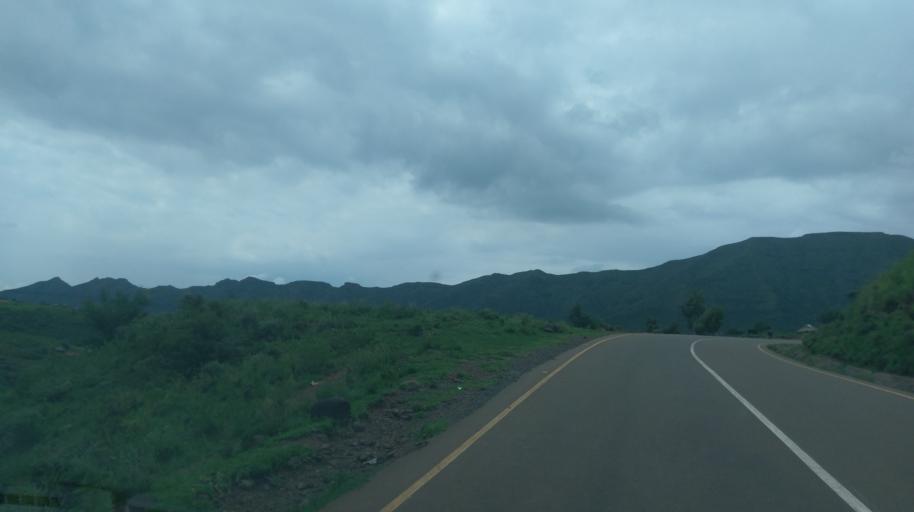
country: LS
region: Butha-Buthe
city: Butha-Buthe
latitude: -29.0464
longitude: 28.3136
